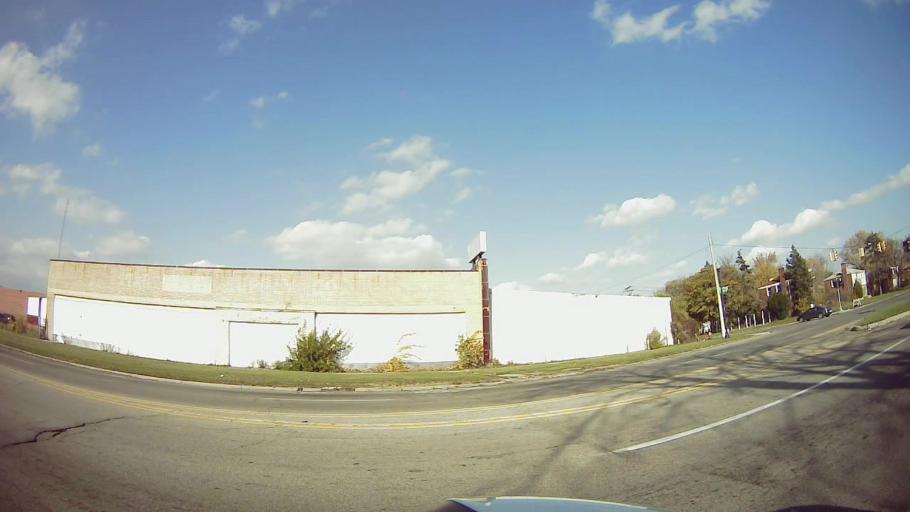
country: US
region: Michigan
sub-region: Macomb County
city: Warren
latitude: 42.4410
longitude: -83.0347
